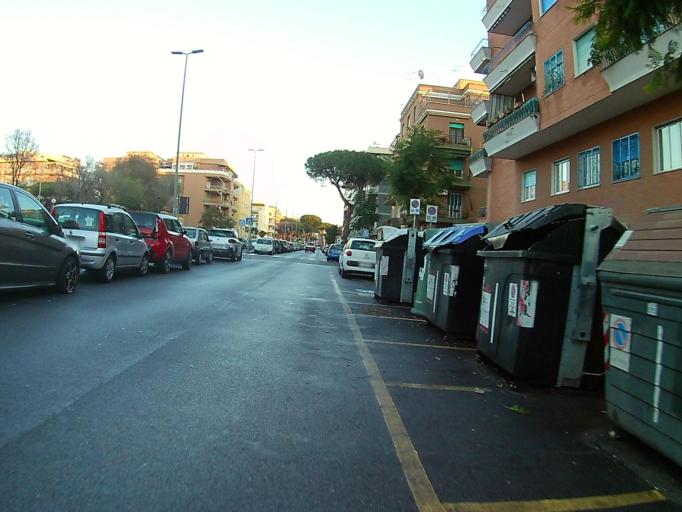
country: IT
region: Latium
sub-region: Citta metropolitana di Roma Capitale
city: Lido di Ostia
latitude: 41.7308
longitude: 12.2864
